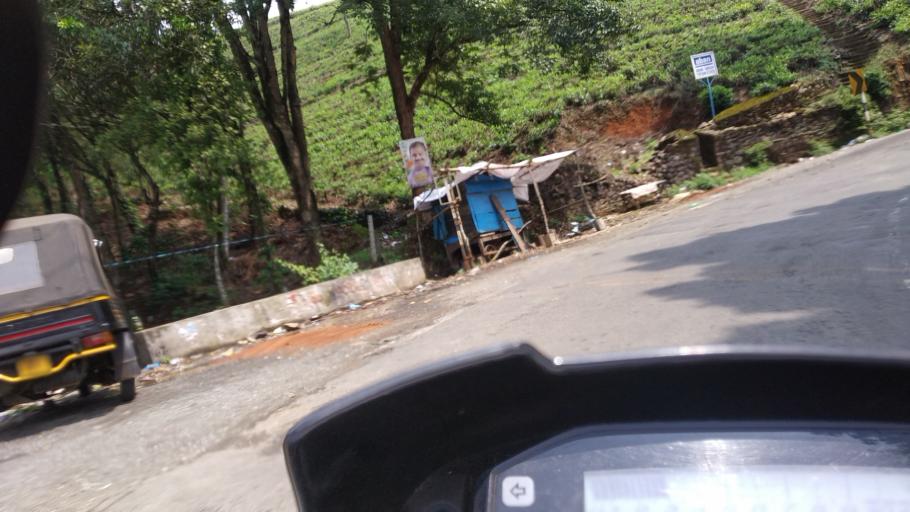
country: IN
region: Kerala
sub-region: Kottayam
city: Erattupetta
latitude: 9.6285
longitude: 76.9794
